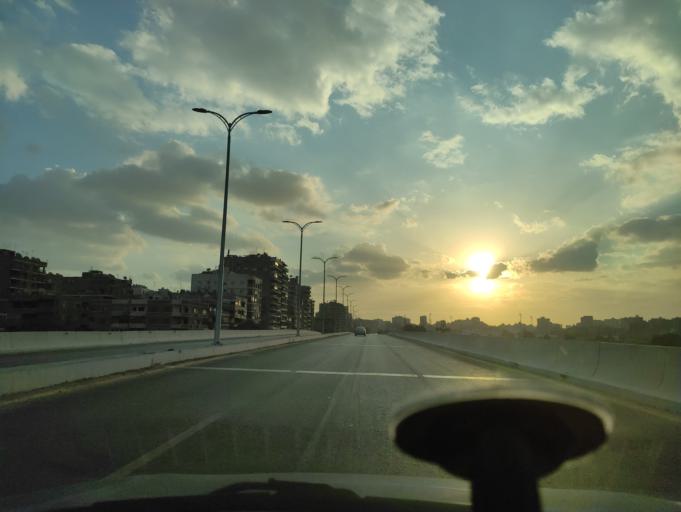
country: EG
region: Muhafazat al Qalyubiyah
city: Al Khankah
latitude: 30.1201
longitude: 31.3516
